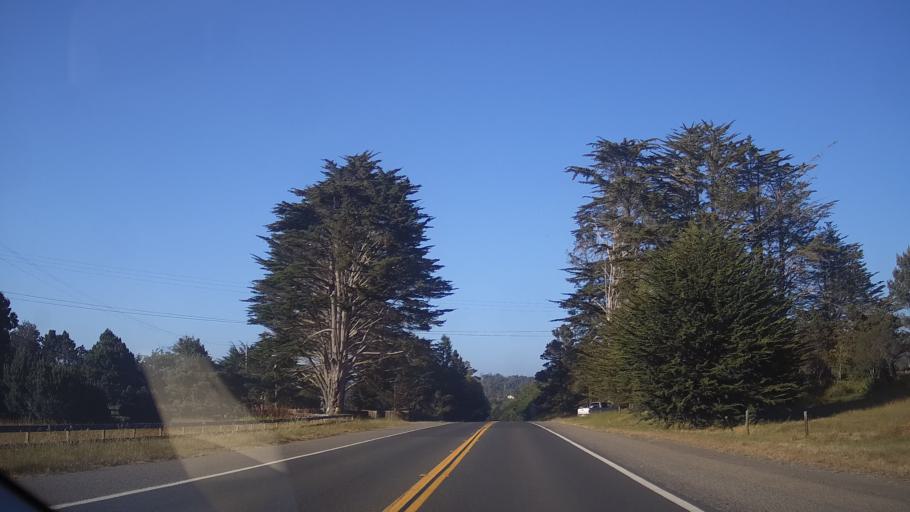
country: US
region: California
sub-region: Mendocino County
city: Fort Bragg
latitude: 39.4841
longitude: -123.7915
